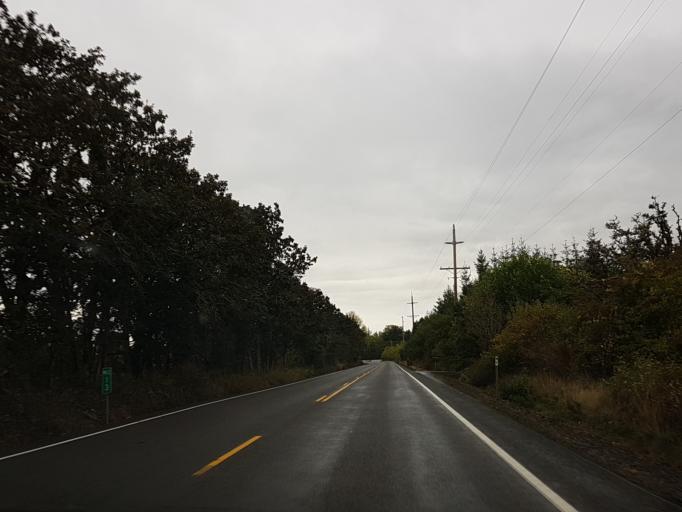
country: US
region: Oregon
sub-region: Marion County
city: Stayton
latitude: 44.7119
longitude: -122.7804
